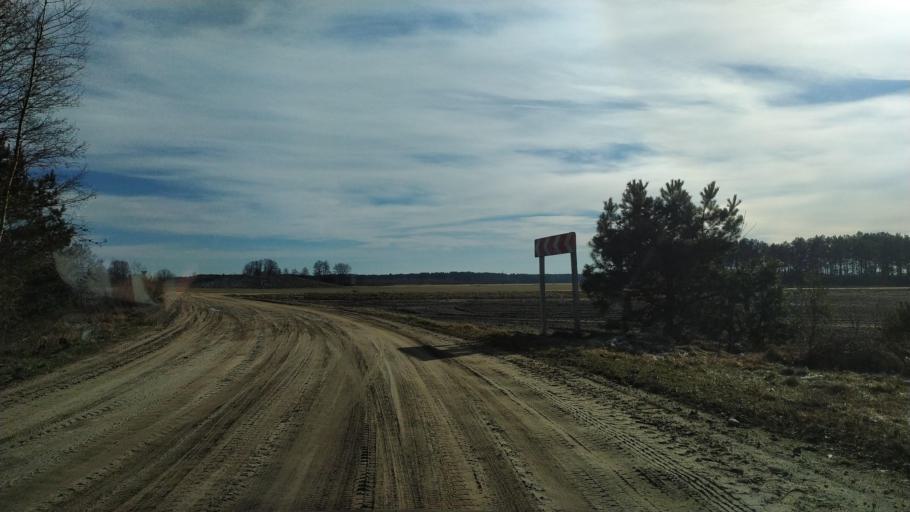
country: BY
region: Brest
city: Pruzhany
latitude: 52.5758
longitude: 24.3019
